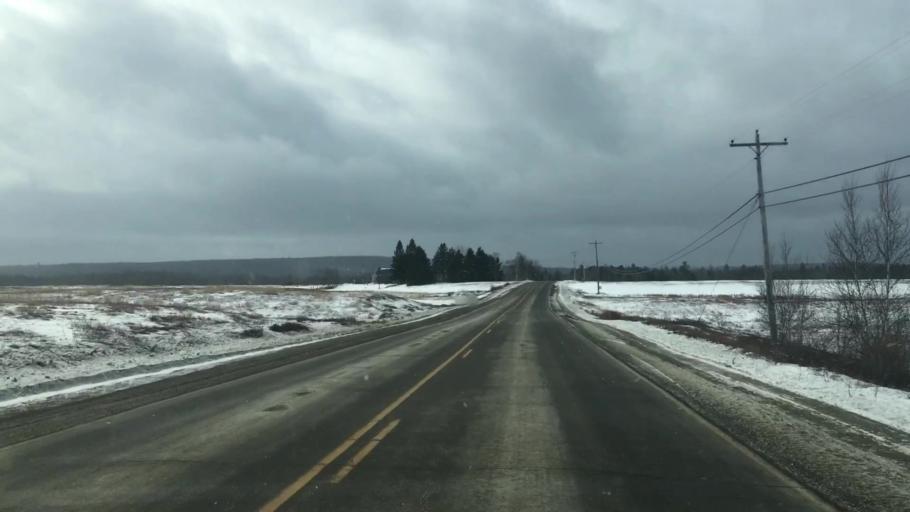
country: US
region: Maine
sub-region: Washington County
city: Calais
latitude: 45.0245
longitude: -67.3759
